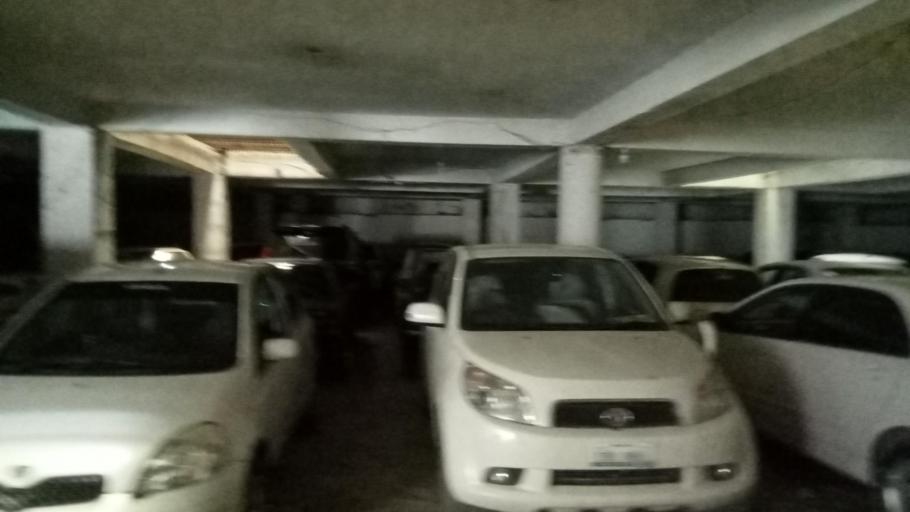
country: PK
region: Khyber Pakhtunkhwa
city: Mingora
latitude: 34.7715
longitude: 72.3631
